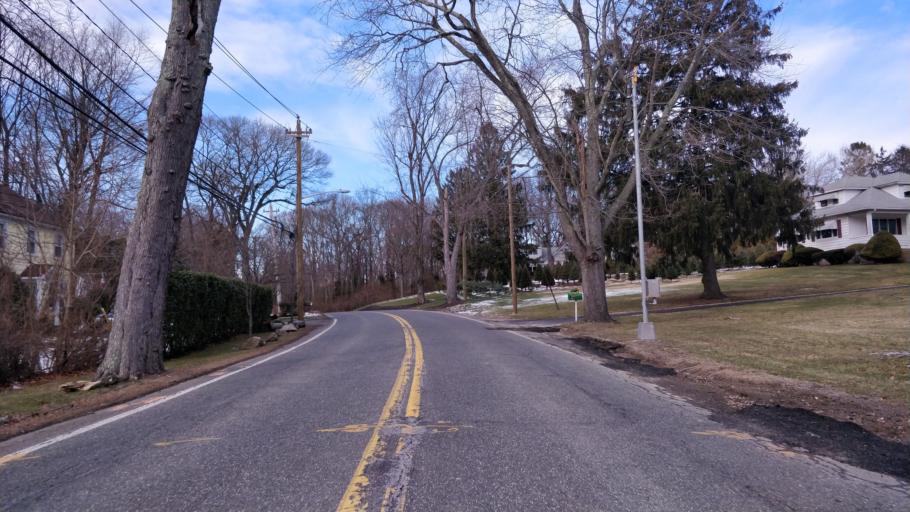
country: US
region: New York
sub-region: Suffolk County
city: Greenlawn
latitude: 40.8753
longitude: -73.3670
